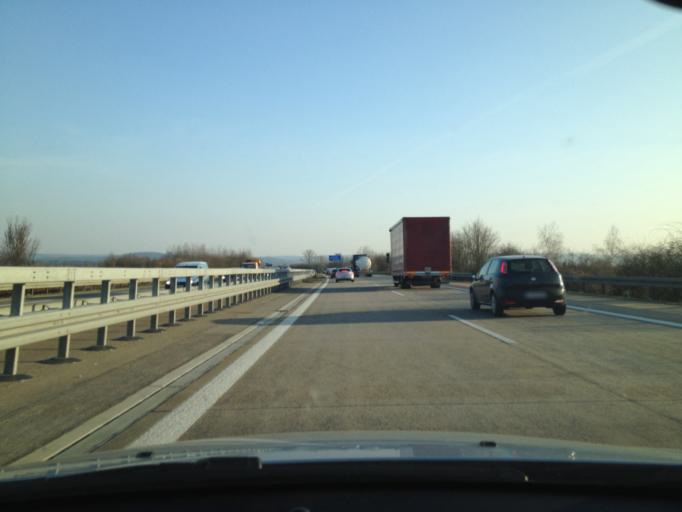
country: DE
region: Baden-Wuerttemberg
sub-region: Regierungsbezirk Stuttgart
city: Ellwangen
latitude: 48.9584
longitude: 10.1851
